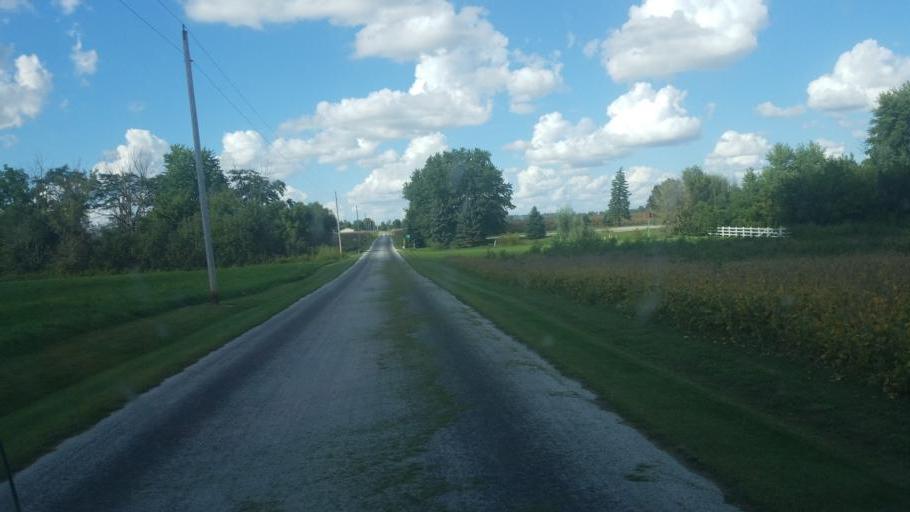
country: US
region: Ohio
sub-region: Hardin County
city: Kenton
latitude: 40.5954
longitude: -83.5232
